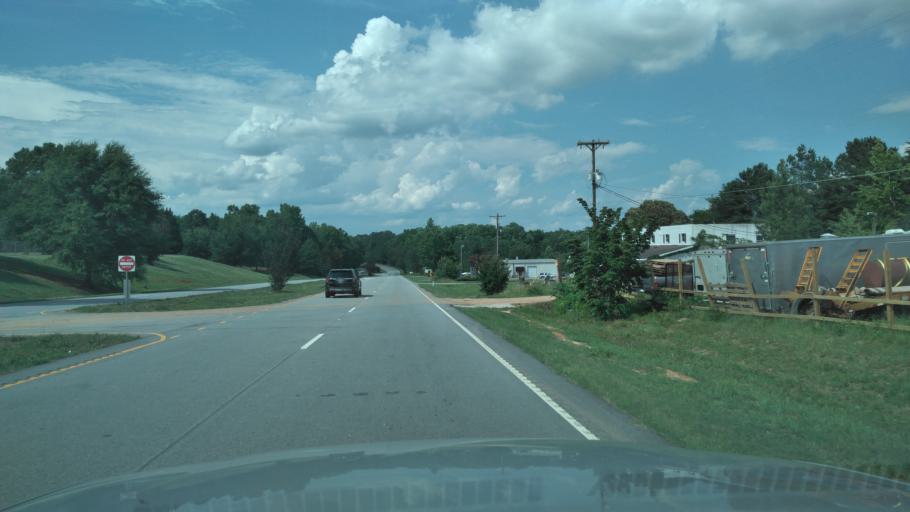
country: US
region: South Carolina
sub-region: Spartanburg County
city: Roebuck
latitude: 34.8748
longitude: -81.9581
